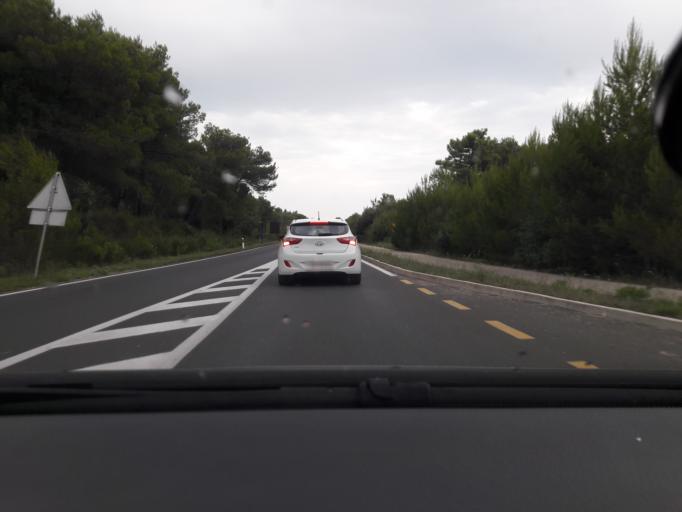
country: HR
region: Zadarska
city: Nin
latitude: 44.1923
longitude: 15.1792
